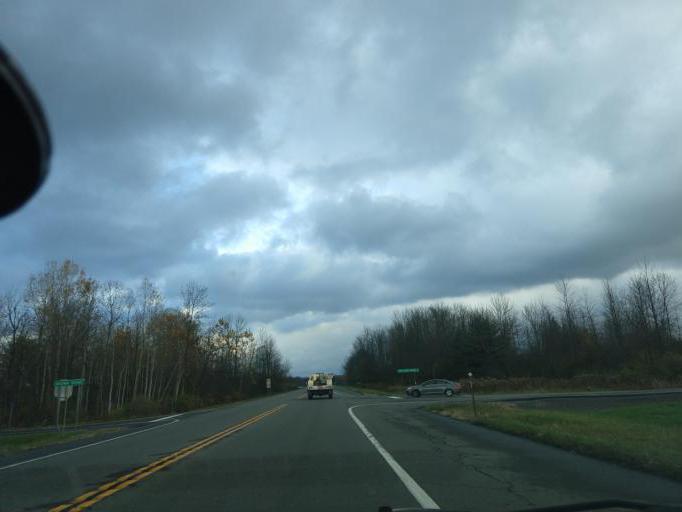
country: US
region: New York
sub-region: Tompkins County
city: Northeast Ithaca
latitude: 42.4828
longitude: -76.4554
